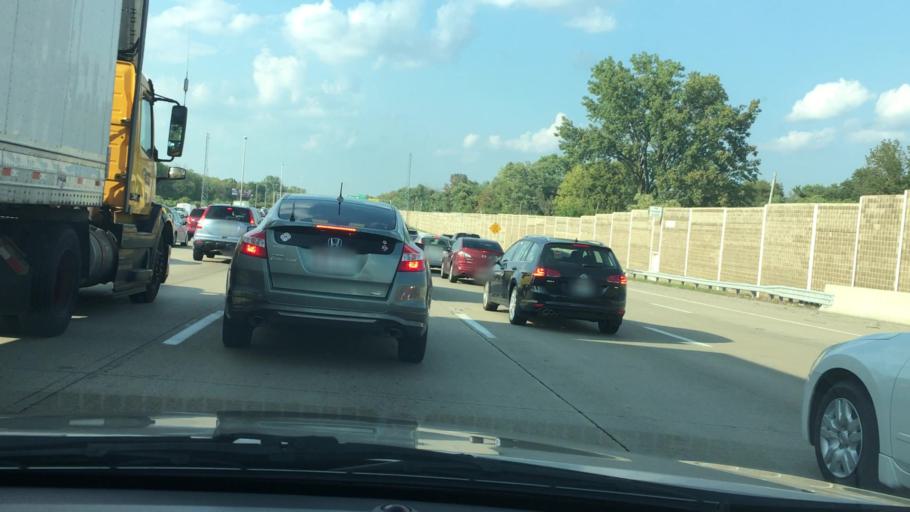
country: US
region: Indiana
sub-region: Marion County
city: Lawrence
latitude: 39.8116
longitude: -86.0307
